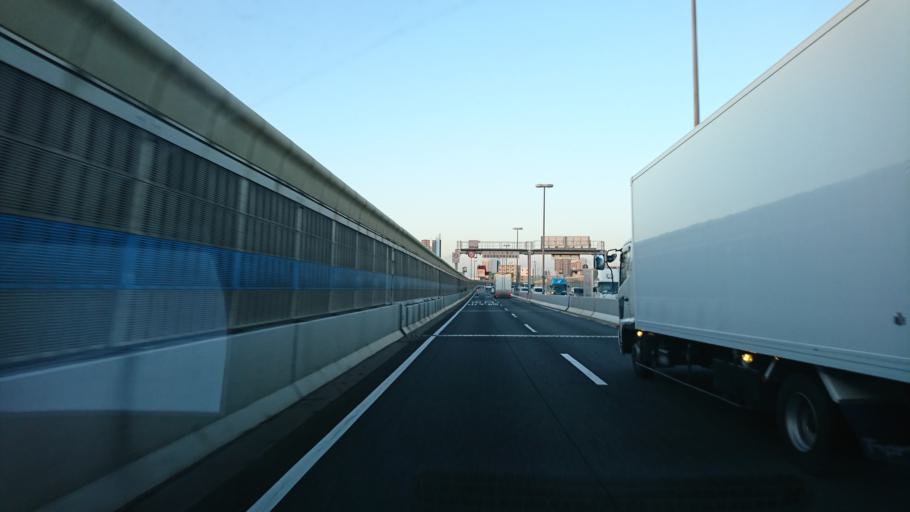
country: JP
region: Hyogo
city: Kobe
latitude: 34.6600
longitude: 135.1561
